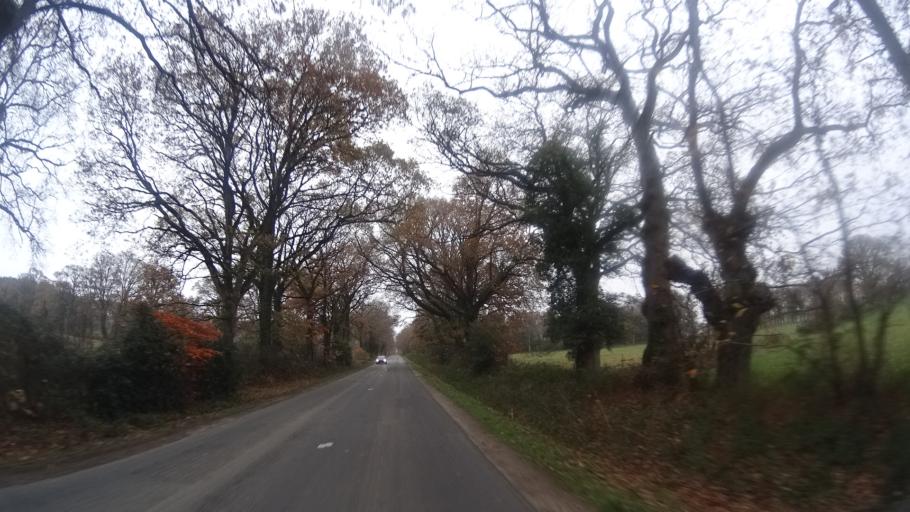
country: FR
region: Brittany
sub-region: Departement d'Ille-et-Vilaine
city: Bains-sur-Oust
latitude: 47.7014
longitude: -2.0556
